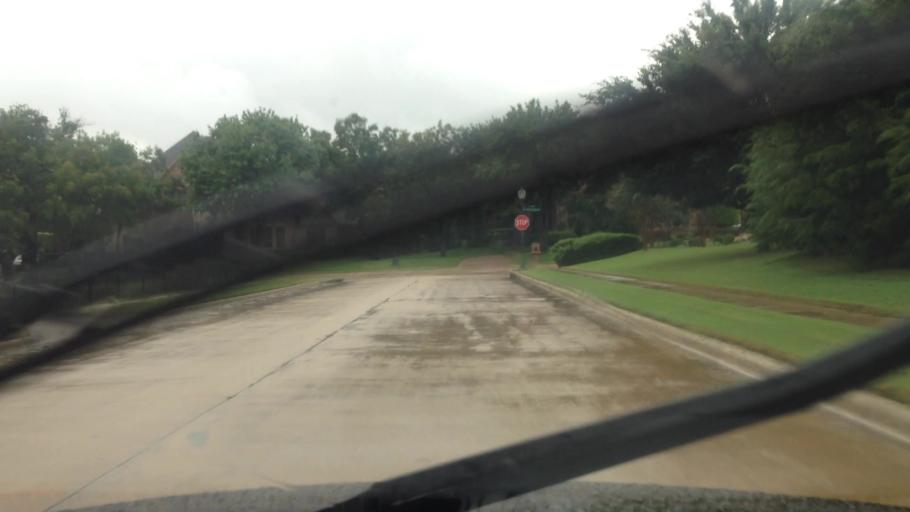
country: US
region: Texas
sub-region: Tarrant County
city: Keller
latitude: 32.9126
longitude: -97.2254
